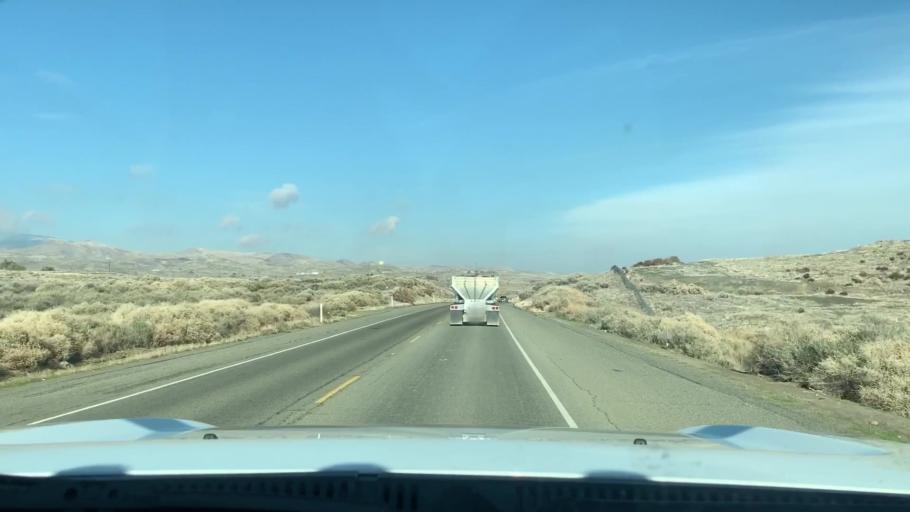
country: US
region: California
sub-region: Fresno County
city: Coalinga
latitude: 36.2259
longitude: -120.3131
